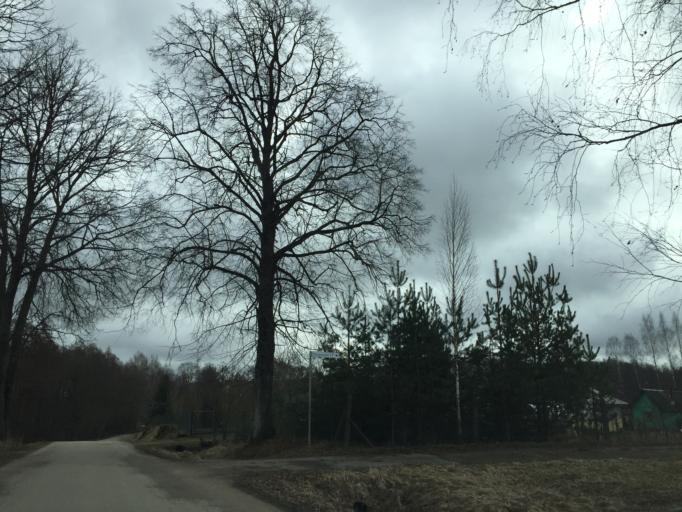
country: LV
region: Ilukste
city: Ilukste
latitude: 55.9066
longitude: 26.3714
